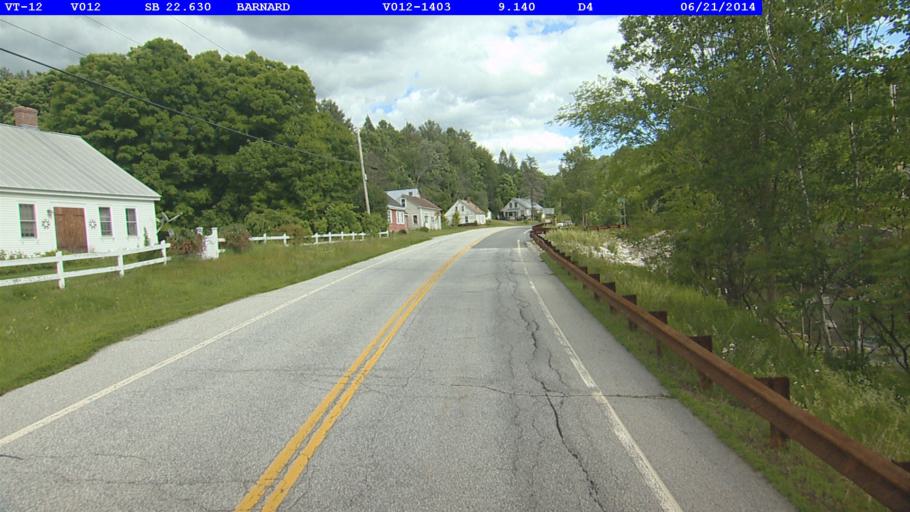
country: US
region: Vermont
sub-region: Orange County
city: Randolph
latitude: 43.7858
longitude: -72.6419
